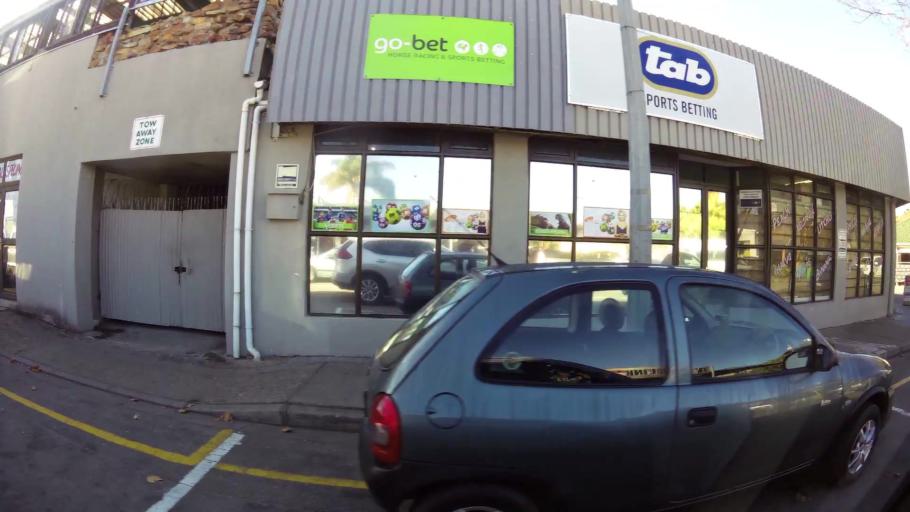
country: ZA
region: Western Cape
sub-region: Eden District Municipality
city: Knysna
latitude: -34.0370
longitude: 23.0461
